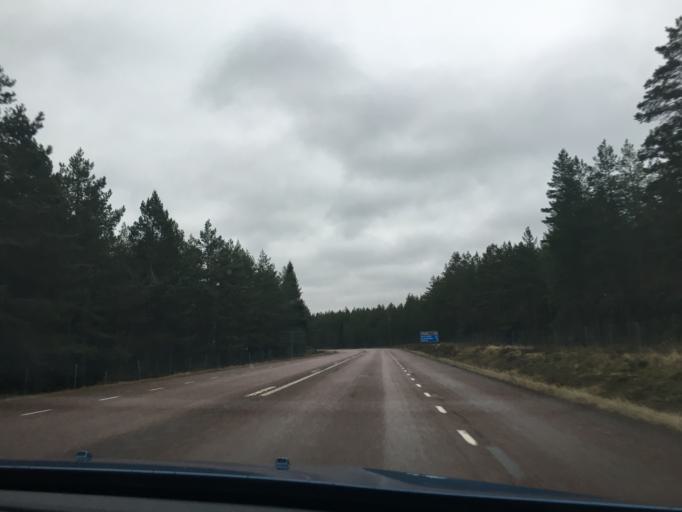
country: SE
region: Uppsala
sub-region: Alvkarleby Kommun
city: AElvkarleby
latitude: 60.4673
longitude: 17.4185
